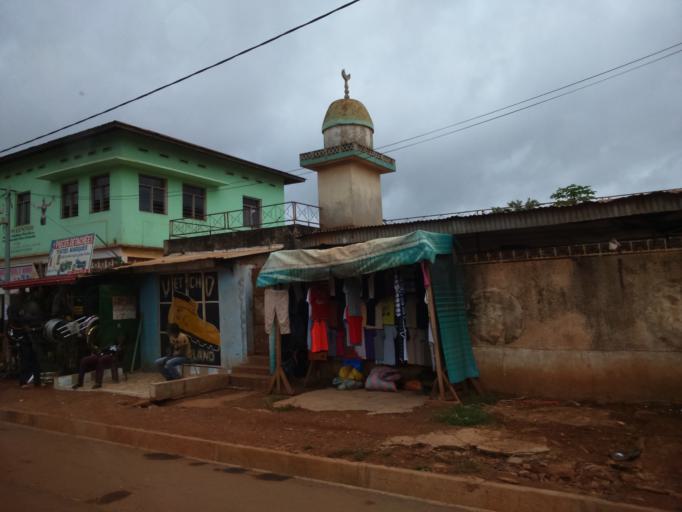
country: CI
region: Moyen-Comoe
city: Abengourou
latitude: 6.7267
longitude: -3.4988
